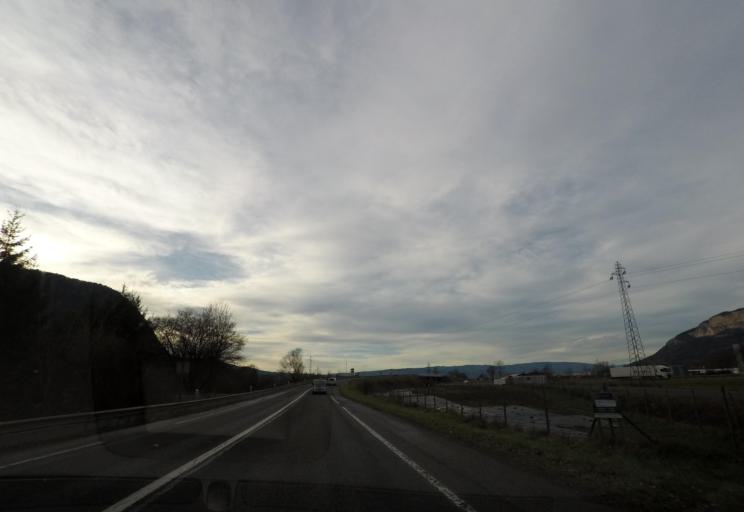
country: FR
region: Rhone-Alpes
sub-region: Departement de la Haute-Savoie
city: Ayse
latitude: 46.0702
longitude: 6.4347
